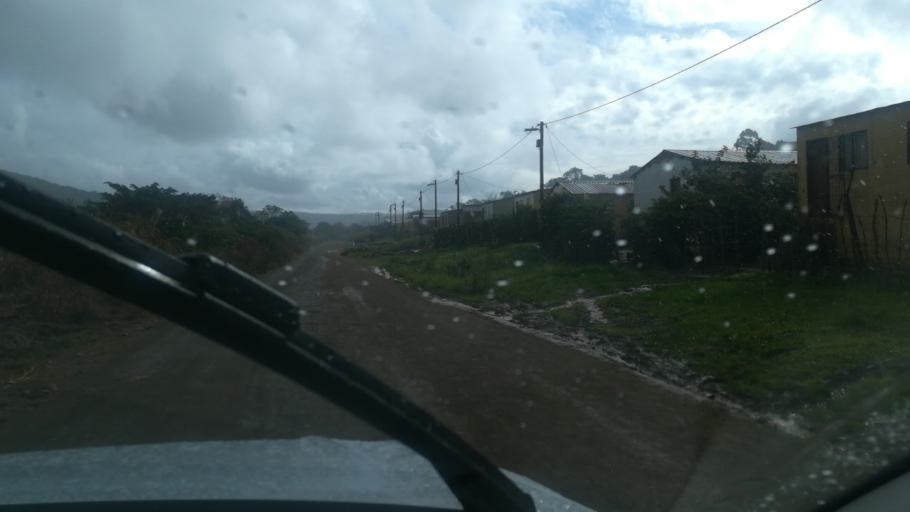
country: ZA
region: Eastern Cape
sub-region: Buffalo City Metropolitan Municipality
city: East London
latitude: -32.9953
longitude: 27.7967
